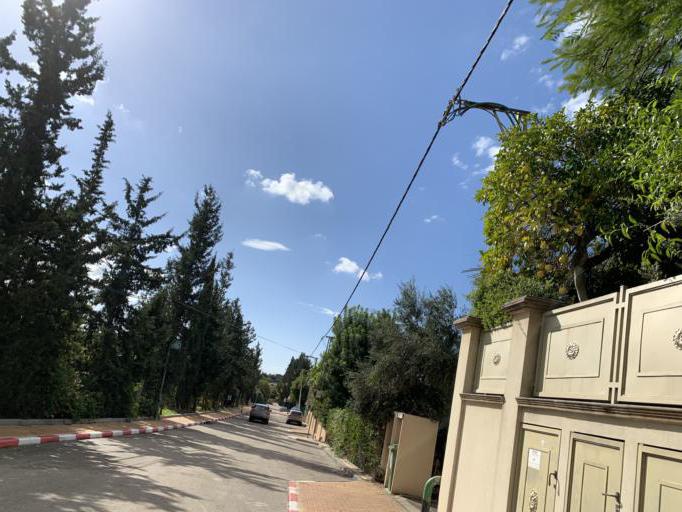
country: IL
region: Central District
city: Hod HaSharon
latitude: 32.1705
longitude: 34.8887
